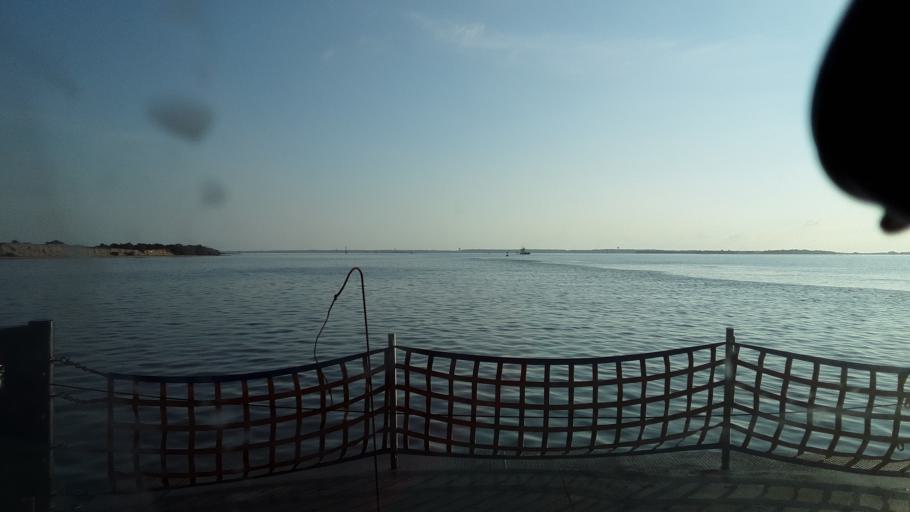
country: US
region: North Carolina
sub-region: Brunswick County
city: Southport
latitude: 33.9504
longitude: -77.9648
